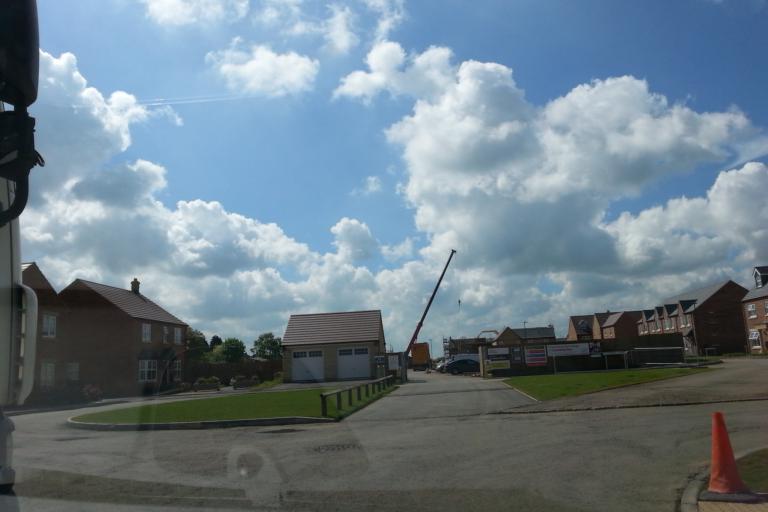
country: GB
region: England
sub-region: District of Rutland
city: Tinwell
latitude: 52.6536
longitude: -0.5054
